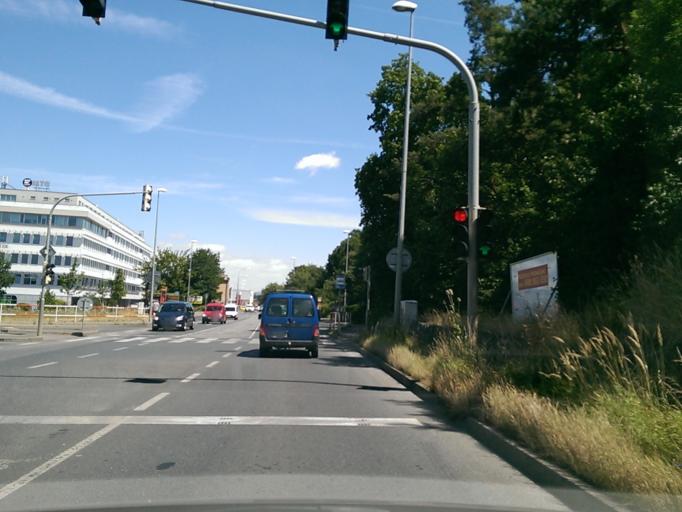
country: CZ
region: Praha
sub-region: Praha 8
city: Liben
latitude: 50.0952
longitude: 14.4756
